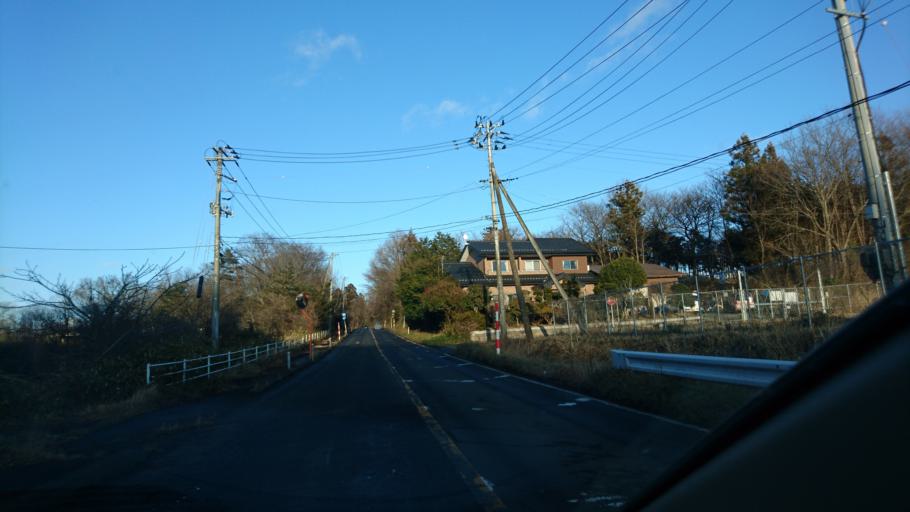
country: JP
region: Miyagi
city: Furukawa
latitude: 38.6124
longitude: 140.8710
